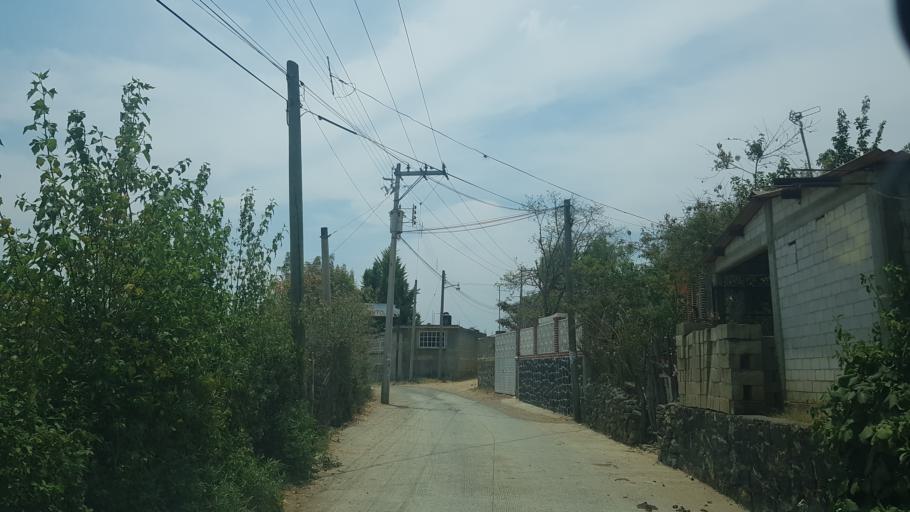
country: MX
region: Puebla
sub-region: Atzitzihuacan
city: Santiago Atzitzihuacan
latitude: 18.8648
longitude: -98.6112
